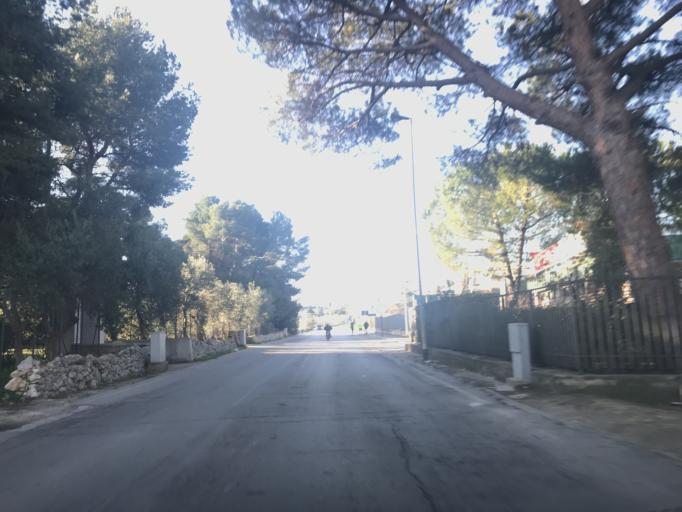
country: IT
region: Apulia
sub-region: Provincia di Bari
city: Corato
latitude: 41.1402
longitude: 16.4155
